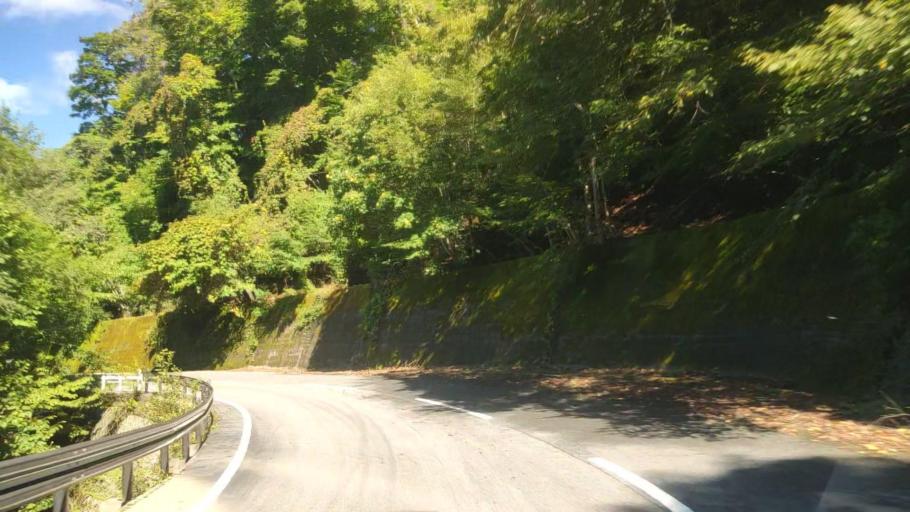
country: JP
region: Yamanashi
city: Fujikawaguchiko
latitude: 35.5614
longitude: 138.7847
